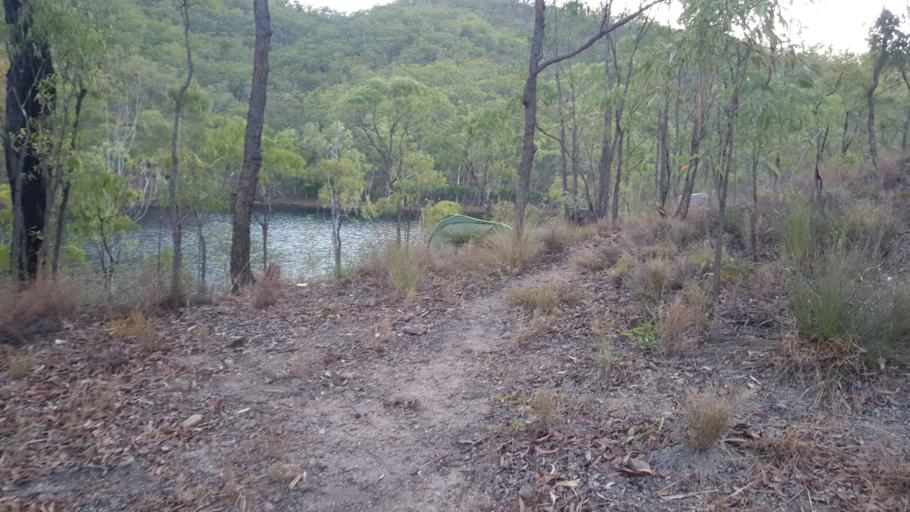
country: AU
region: Queensland
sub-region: Tablelands
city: Atherton
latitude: -17.4046
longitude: 145.2294
